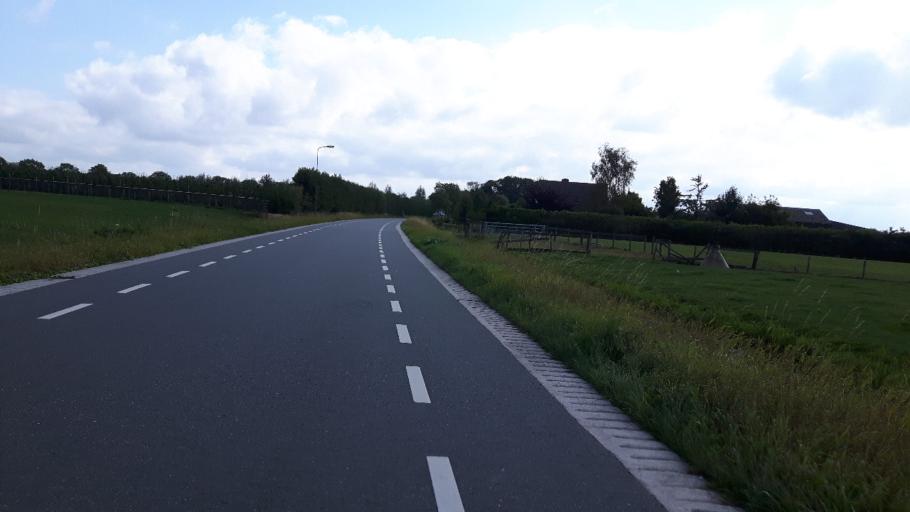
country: NL
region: Utrecht
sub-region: Stichtse Vecht
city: Spechtenkamp
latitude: 52.1009
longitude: 4.9904
